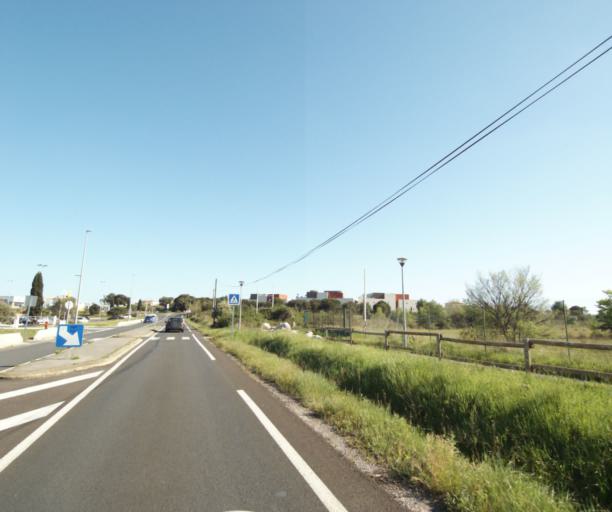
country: FR
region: Languedoc-Roussillon
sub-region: Departement de l'Herault
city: Perols
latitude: 43.5717
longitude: 3.9389
